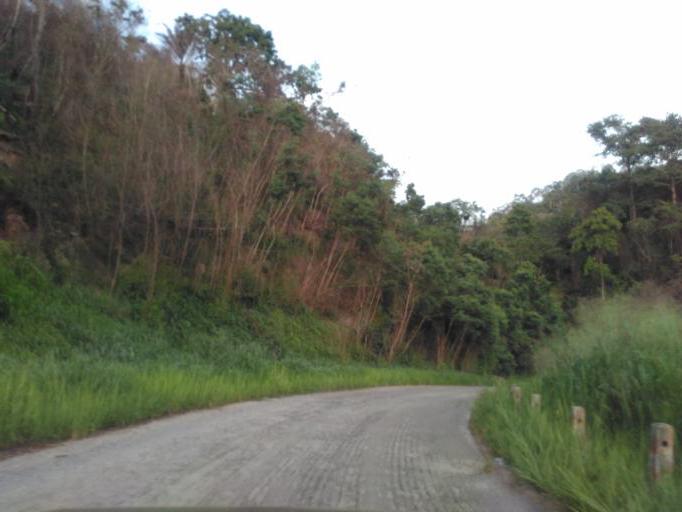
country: GH
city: Bekwai
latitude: 6.5510
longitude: -1.4262
